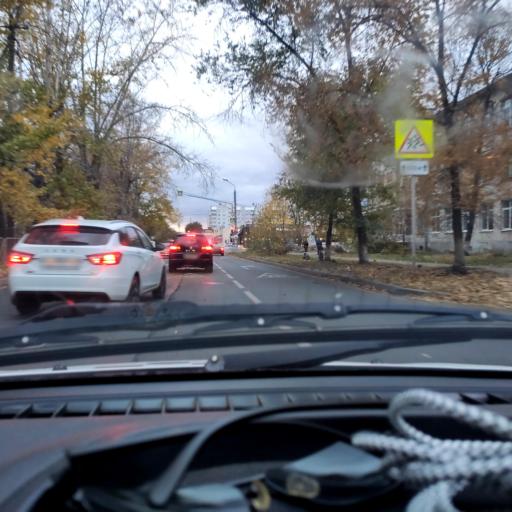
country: RU
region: Samara
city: Tol'yatti
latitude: 53.5178
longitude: 49.4267
